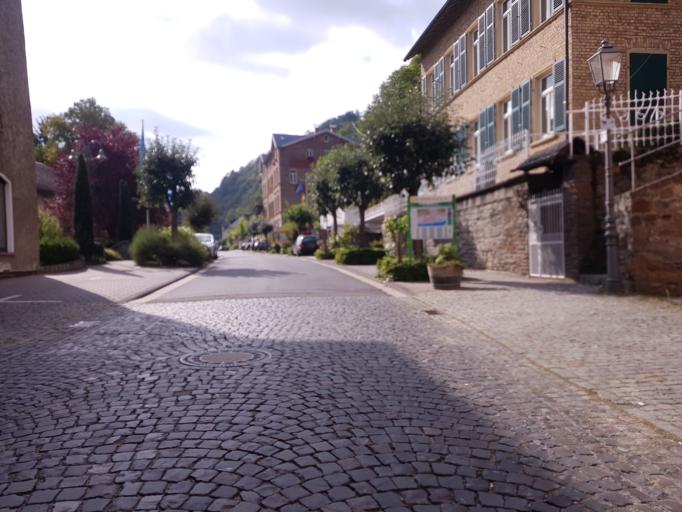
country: DE
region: Rheinland-Pfalz
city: Bacharach
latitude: 50.0575
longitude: 7.7684
